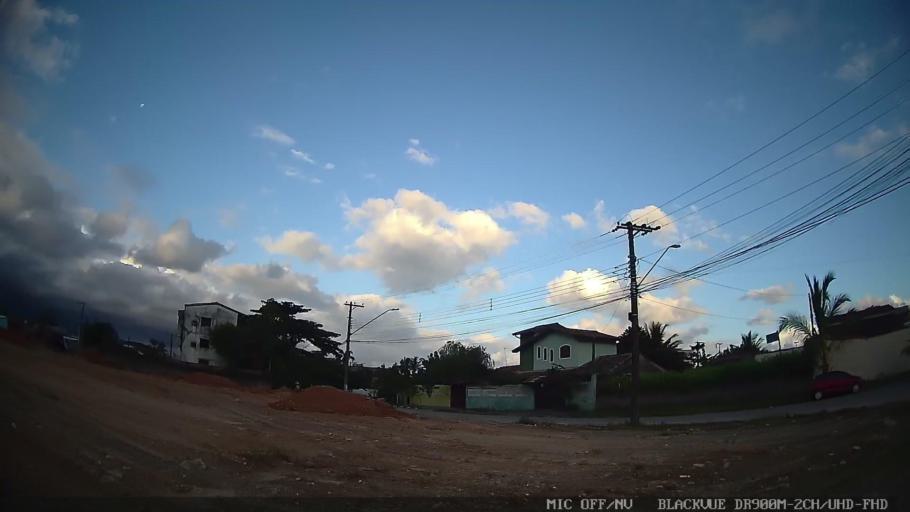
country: BR
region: Sao Paulo
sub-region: Caraguatatuba
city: Caraguatatuba
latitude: -23.6629
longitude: -45.4482
